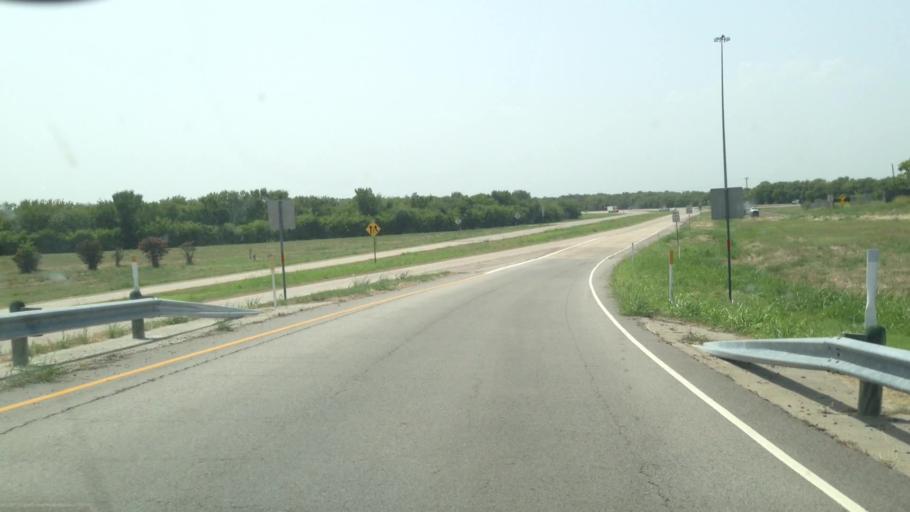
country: US
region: Texas
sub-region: Hunt County
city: Greenville
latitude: 33.1364
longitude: -96.0735
